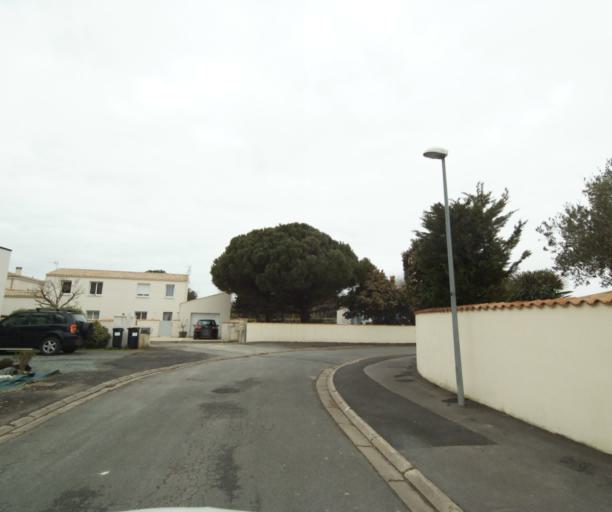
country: FR
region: Poitou-Charentes
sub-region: Departement de la Charente-Maritime
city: Lagord
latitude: 46.1919
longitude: -1.1549
